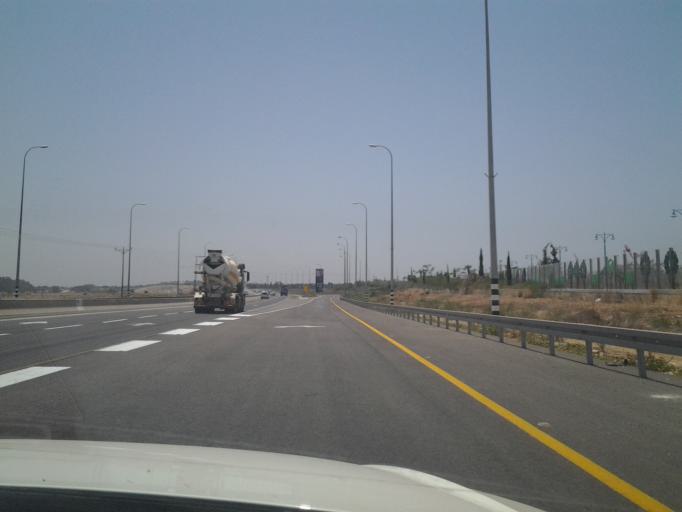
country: IL
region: Haifa
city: Hadera
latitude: 32.4310
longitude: 34.8882
